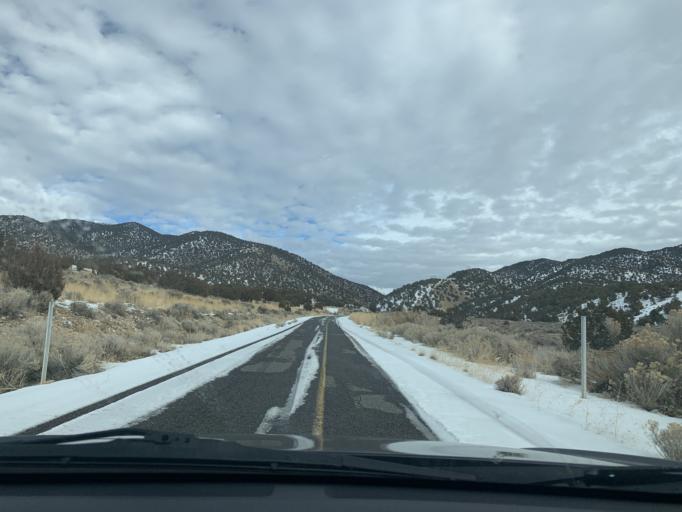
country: US
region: Utah
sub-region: Tooele County
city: Tooele
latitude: 40.3055
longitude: -112.2607
